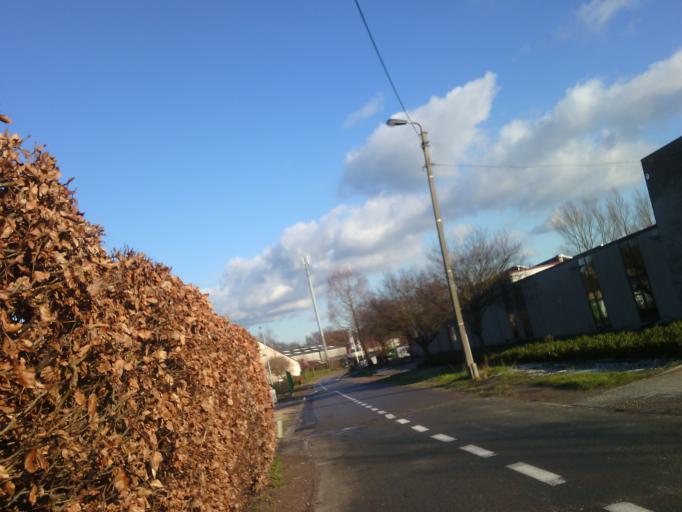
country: BE
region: Flanders
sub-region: Provincie Oost-Vlaanderen
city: Berlare
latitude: 51.0197
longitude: 3.9956
